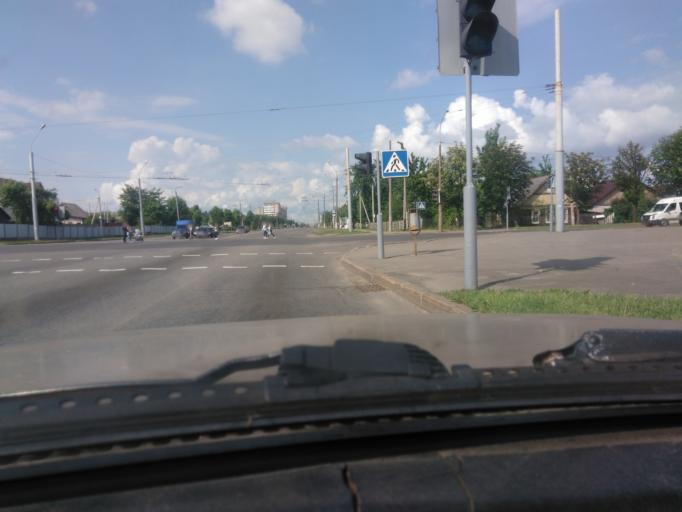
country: BY
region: Mogilev
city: Mahilyow
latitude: 53.9272
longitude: 30.3505
